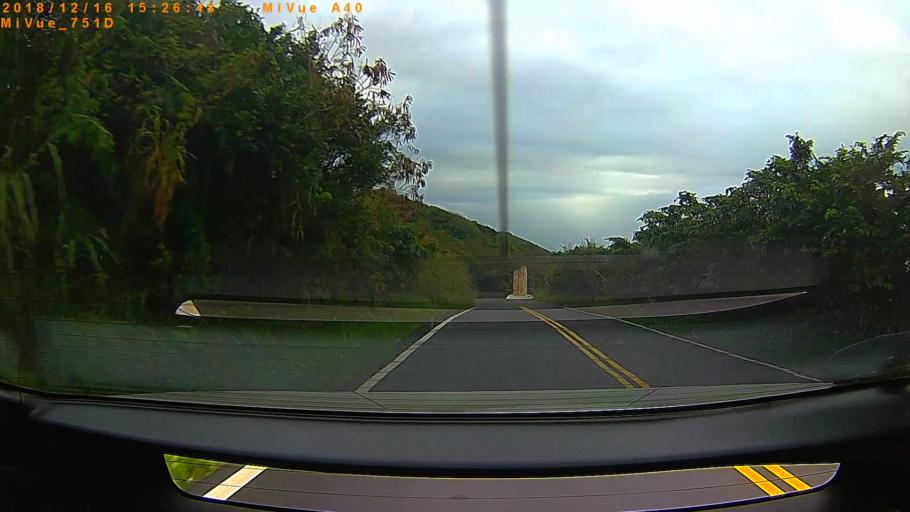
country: TW
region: Taiwan
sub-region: Hualien
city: Hualian
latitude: 23.9243
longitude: 121.6052
